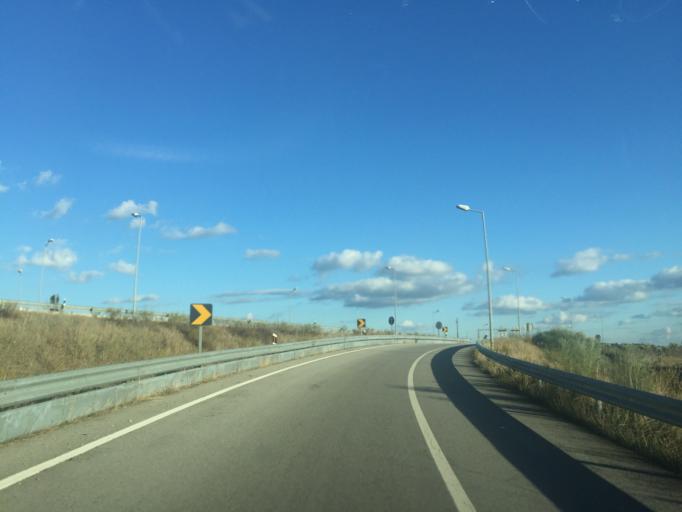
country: PT
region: Portalegre
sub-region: Alter do Chao
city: Alter do Chao
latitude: 39.1971
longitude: -7.6971
